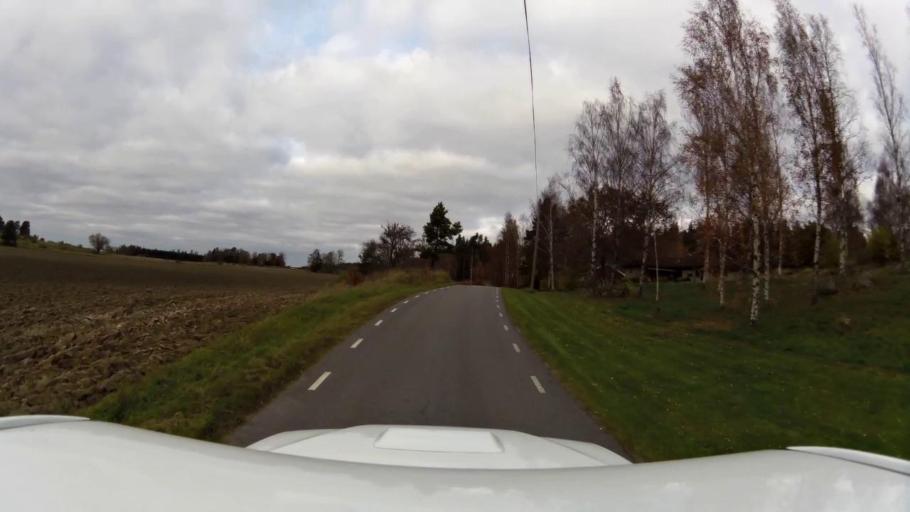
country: SE
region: OEstergoetland
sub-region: Linkopings Kommun
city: Linghem
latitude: 58.3868
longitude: 15.8147
